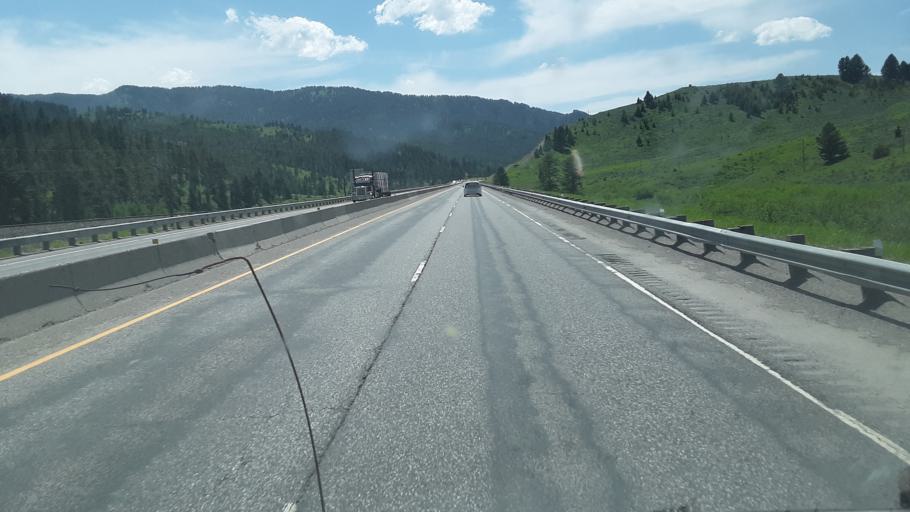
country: US
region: Montana
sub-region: Gallatin County
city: Bozeman
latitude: 45.6525
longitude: -110.8554
